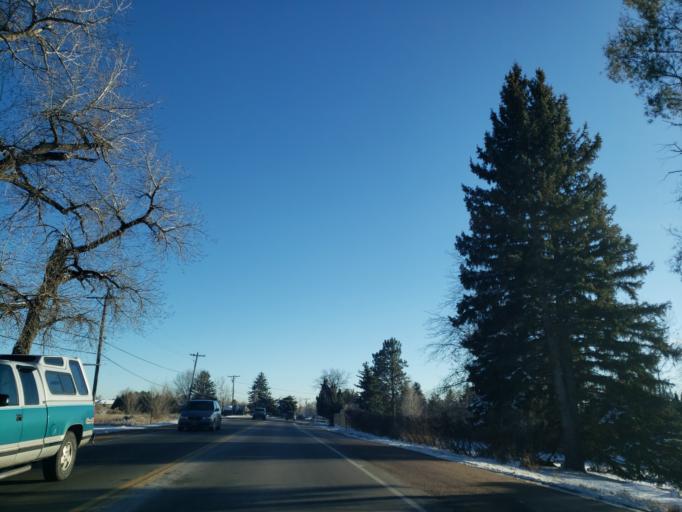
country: US
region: Colorado
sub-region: Larimer County
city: Fort Collins
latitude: 40.6286
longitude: -105.0711
